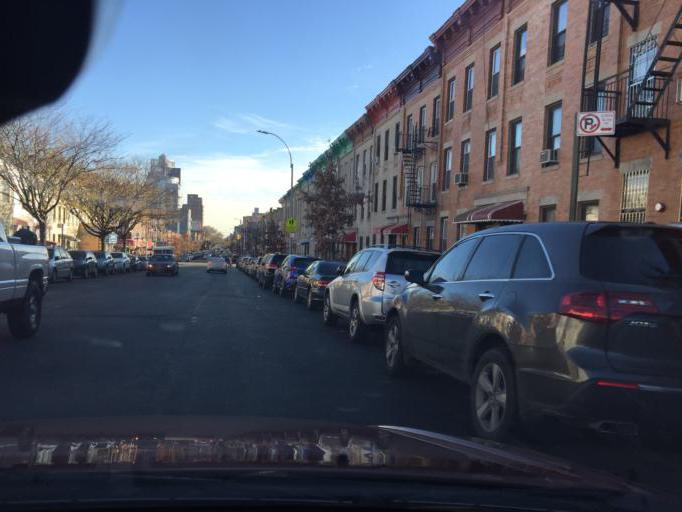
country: US
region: New York
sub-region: Kings County
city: Bensonhurst
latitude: 40.6375
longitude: -74.0129
